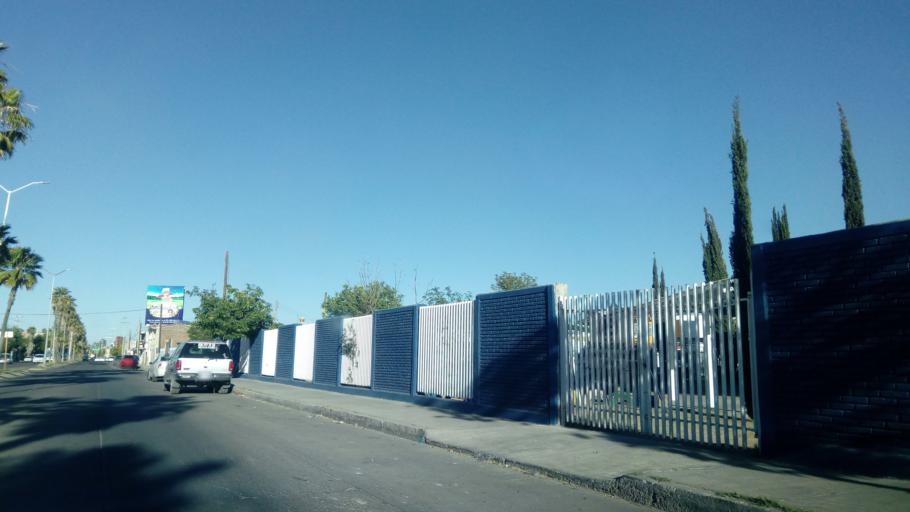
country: MX
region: Durango
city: Victoria de Durango
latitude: 24.0109
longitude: -104.6889
